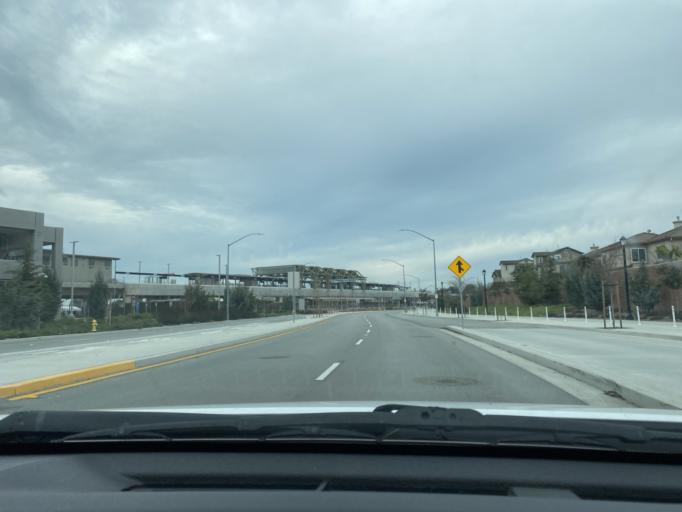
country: US
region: California
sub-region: Santa Clara County
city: San Jose
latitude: 37.3671
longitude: -121.8728
